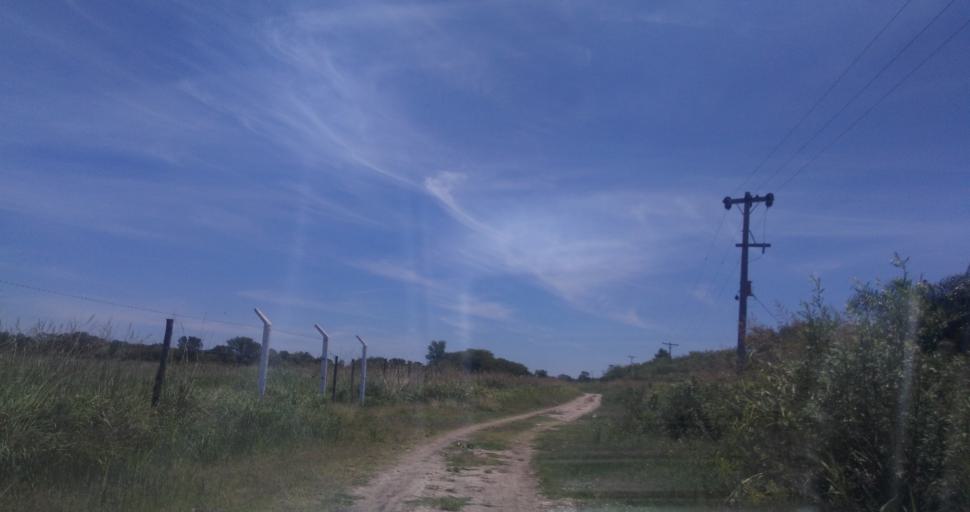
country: AR
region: Chaco
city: Fontana
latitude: -27.4338
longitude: -59.0365
